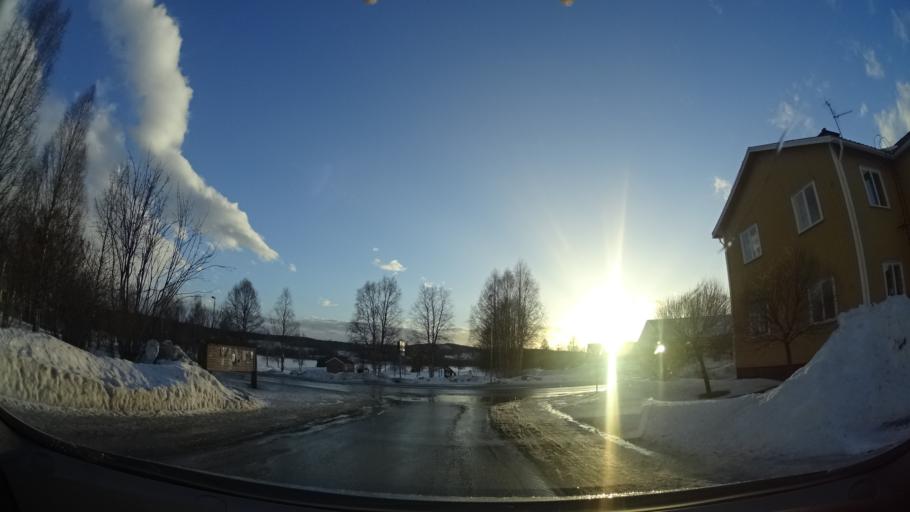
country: SE
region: Vaesterbotten
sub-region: Mala Kommun
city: Mala
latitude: 65.1817
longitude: 18.7447
